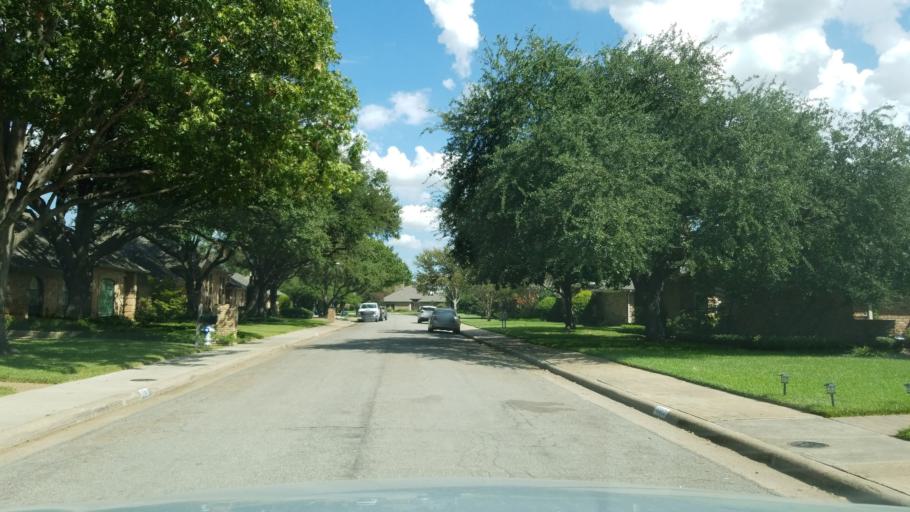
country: US
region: Texas
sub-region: Dallas County
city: Addison
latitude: 32.9605
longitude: -96.7996
